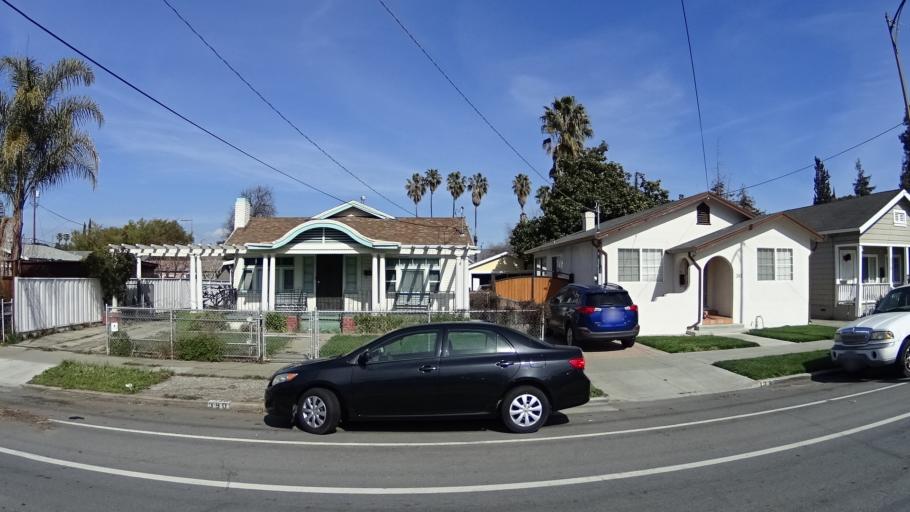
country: US
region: California
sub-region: Santa Clara County
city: San Jose
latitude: 37.3453
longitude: -121.8888
